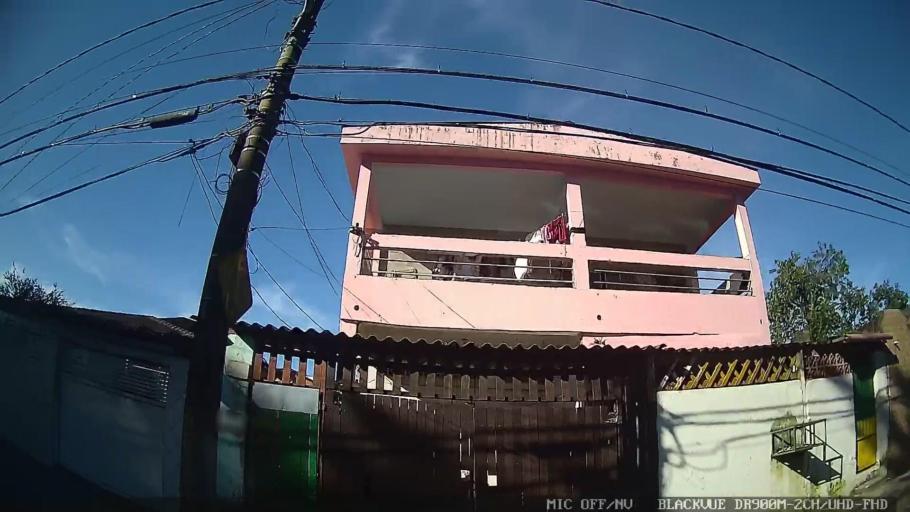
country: BR
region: Sao Paulo
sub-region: Guaruja
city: Guaruja
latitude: -23.9450
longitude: -46.2812
